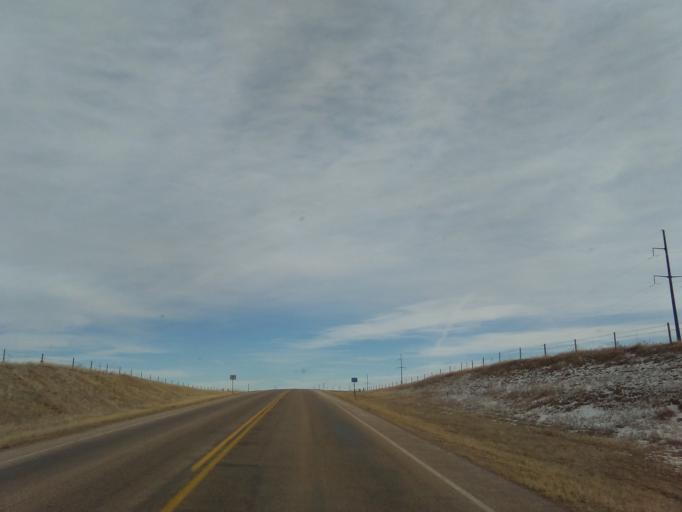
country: US
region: Wyoming
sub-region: Laramie County
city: Ranchettes
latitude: 41.3834
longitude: -104.5197
